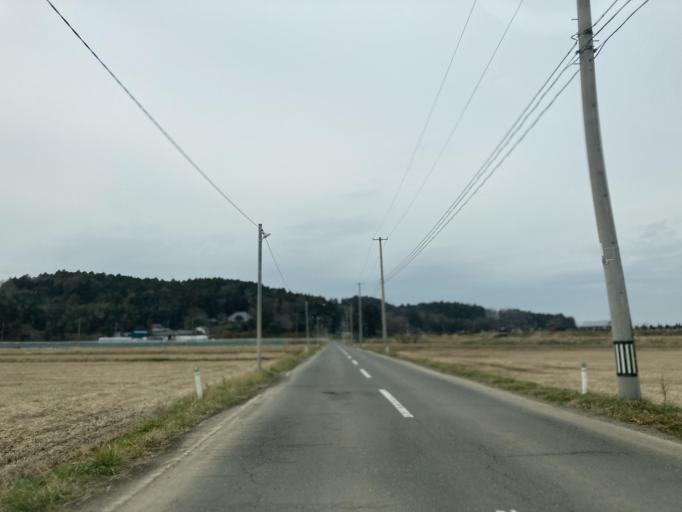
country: JP
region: Miyagi
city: Wakuya
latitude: 38.6915
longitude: 141.2728
